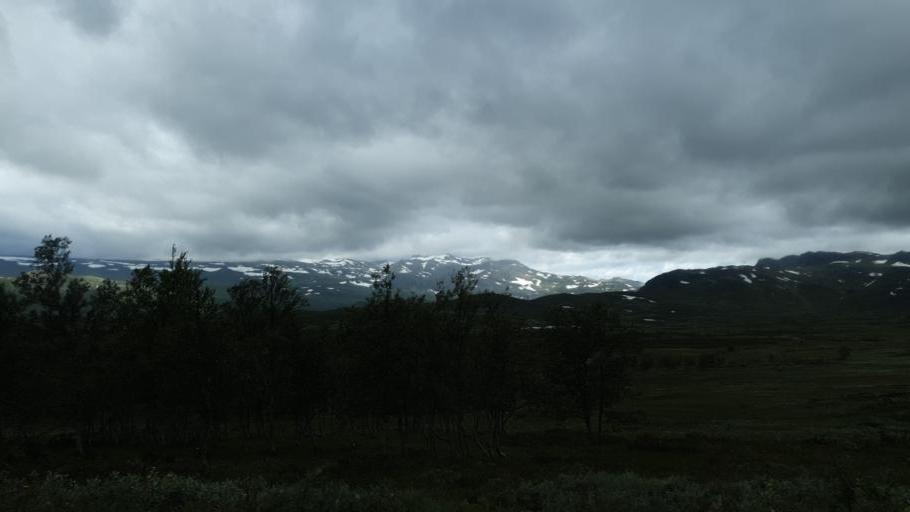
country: NO
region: Oppland
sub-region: Vestre Slidre
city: Slidre
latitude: 61.2686
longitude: 8.8635
